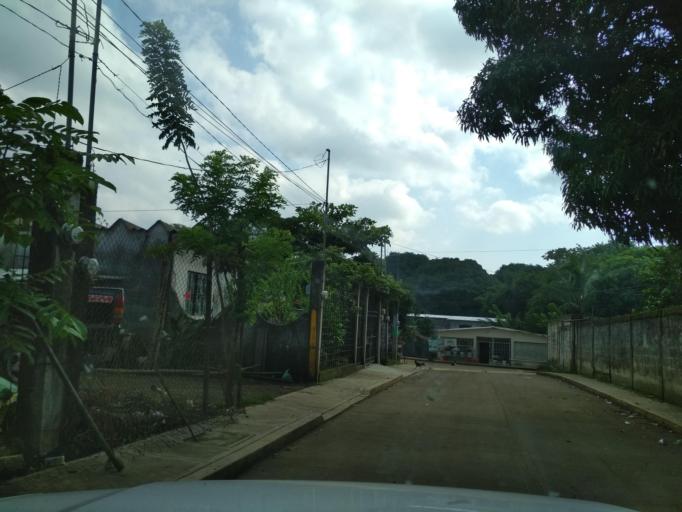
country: MX
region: Veracruz
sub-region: San Andres Tuxtla
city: Matacapan
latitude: 18.4390
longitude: -95.1760
